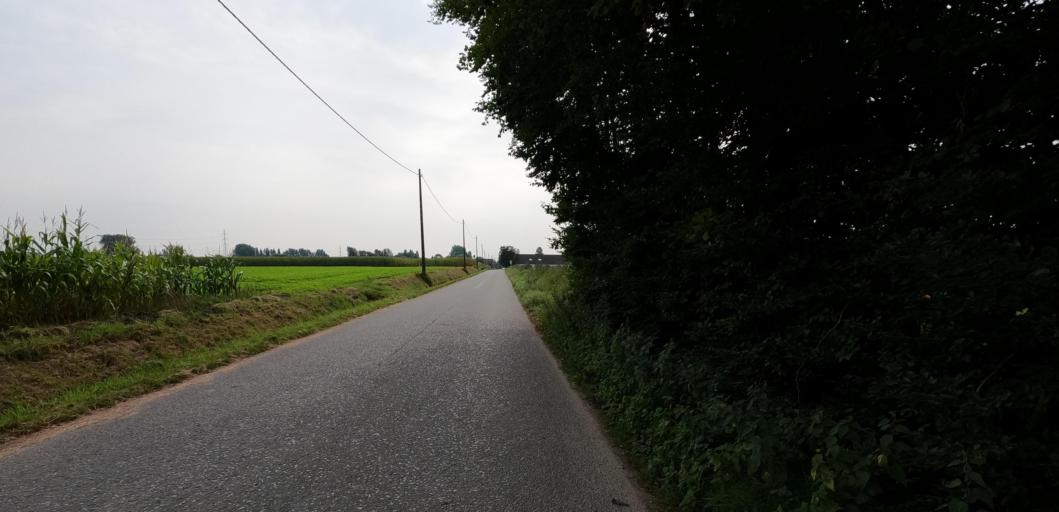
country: BE
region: Flanders
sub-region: Provincie Oost-Vlaanderen
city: Buggenhout
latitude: 50.9959
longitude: 4.2263
